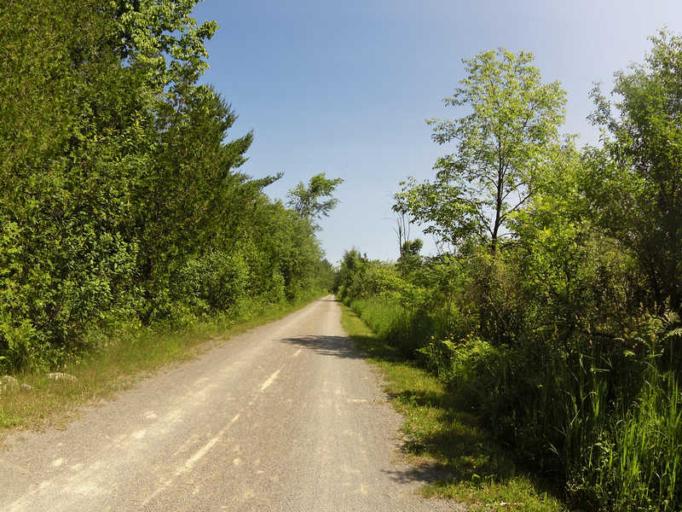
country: CA
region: Ontario
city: Peterborough
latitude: 44.3670
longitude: -78.2875
